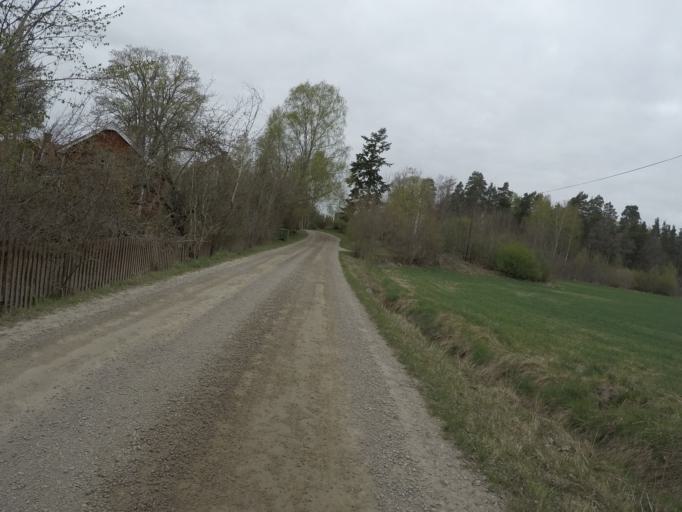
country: SE
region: Soedermanland
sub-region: Eskilstuna Kommun
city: Kvicksund
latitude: 59.4361
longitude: 16.2949
